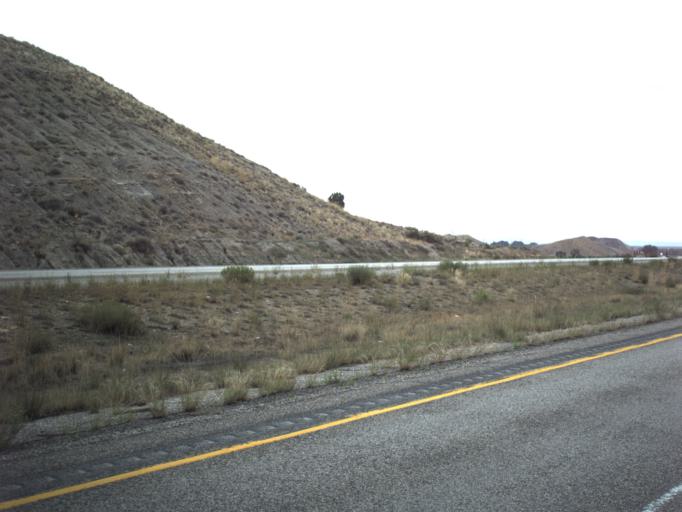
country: US
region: Utah
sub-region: Carbon County
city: Carbonville
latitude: 39.6303
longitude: -110.8621
